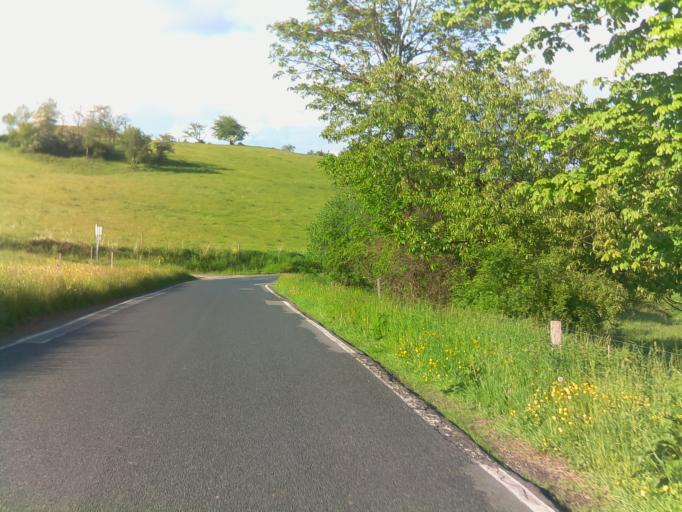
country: DE
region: Thuringia
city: Oberhain
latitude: 50.6387
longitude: 11.1362
